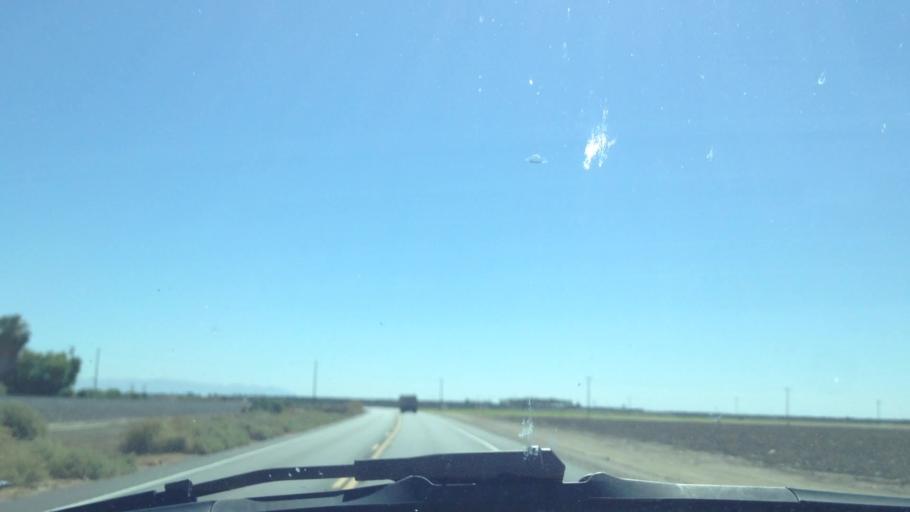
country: US
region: California
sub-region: Riverside County
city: Mecca
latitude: 33.5397
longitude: -116.0287
